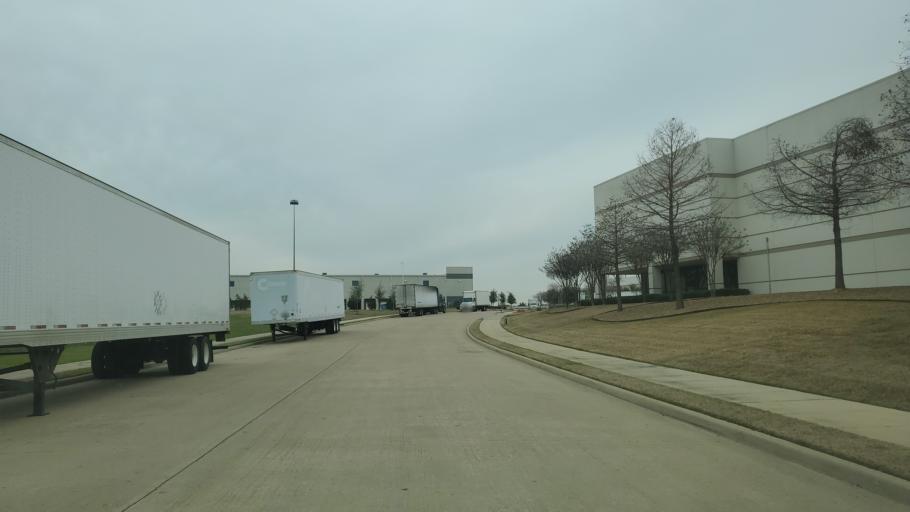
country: US
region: Texas
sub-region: Dallas County
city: Coppell
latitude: 32.9862
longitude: -97.0197
